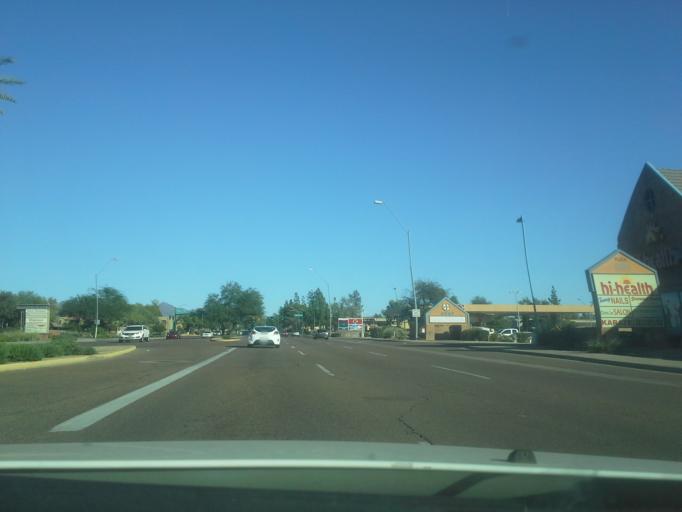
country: US
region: Arizona
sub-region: Maricopa County
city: Paradise Valley
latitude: 33.6261
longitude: -111.9799
